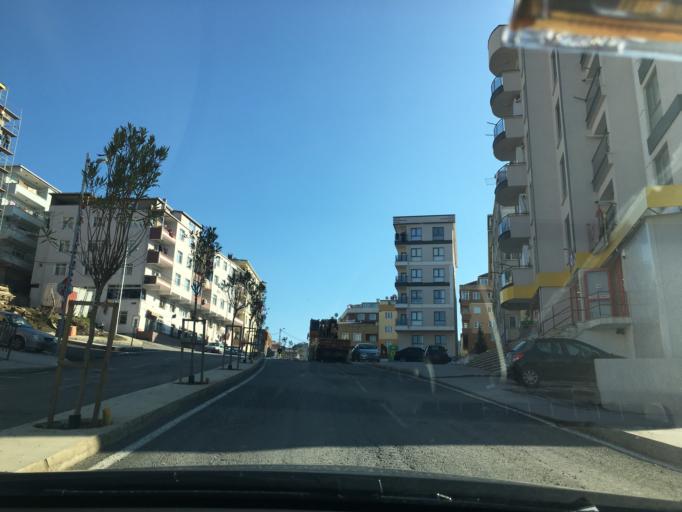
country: TR
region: Istanbul
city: Icmeler
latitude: 40.8691
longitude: 29.3025
